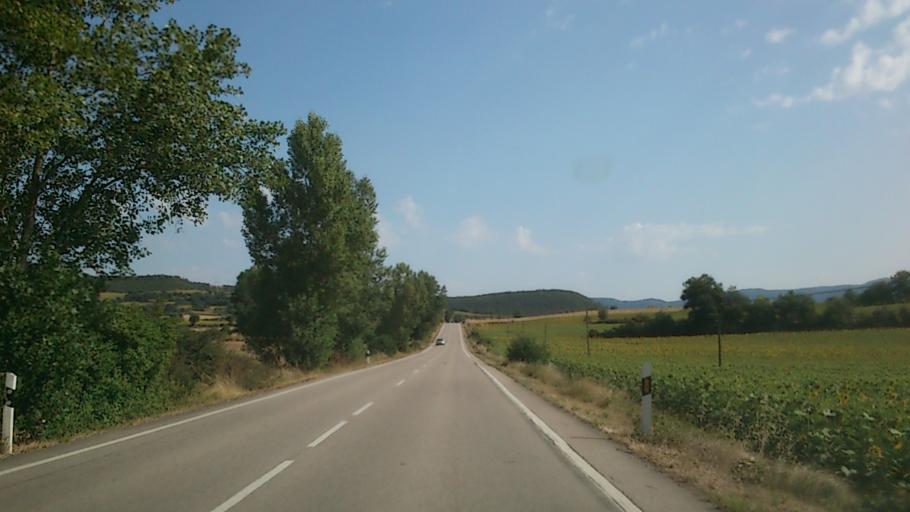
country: ES
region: Castille and Leon
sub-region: Provincia de Burgos
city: Trespaderne
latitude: 42.8246
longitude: -3.3623
